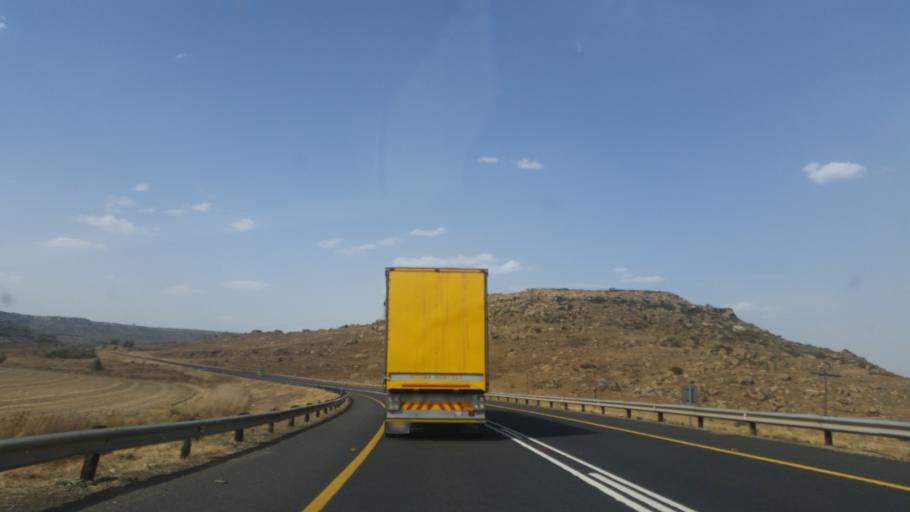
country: ZA
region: Orange Free State
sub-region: Thabo Mofutsanyana District Municipality
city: Bethlehem
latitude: -28.3073
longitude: 28.5007
